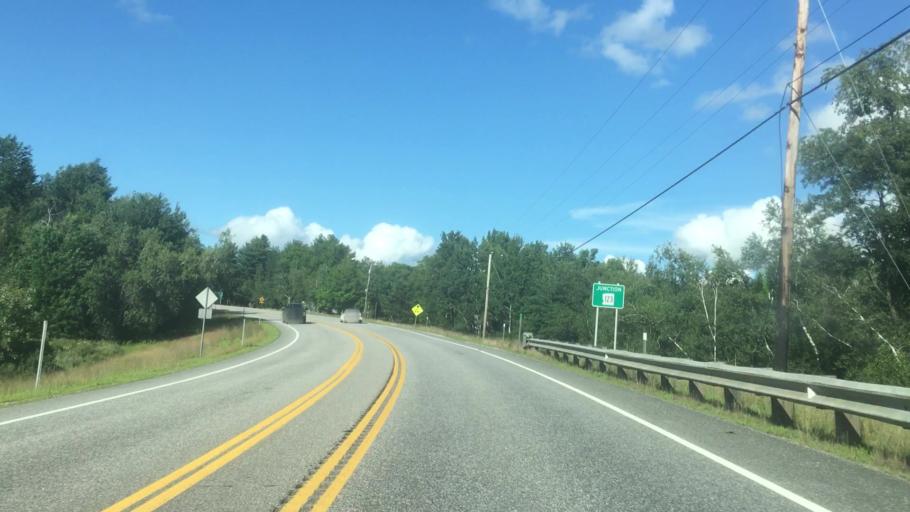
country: US
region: New Hampshire
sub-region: Cheshire County
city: Harrisville
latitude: 43.0392
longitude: -72.0747
